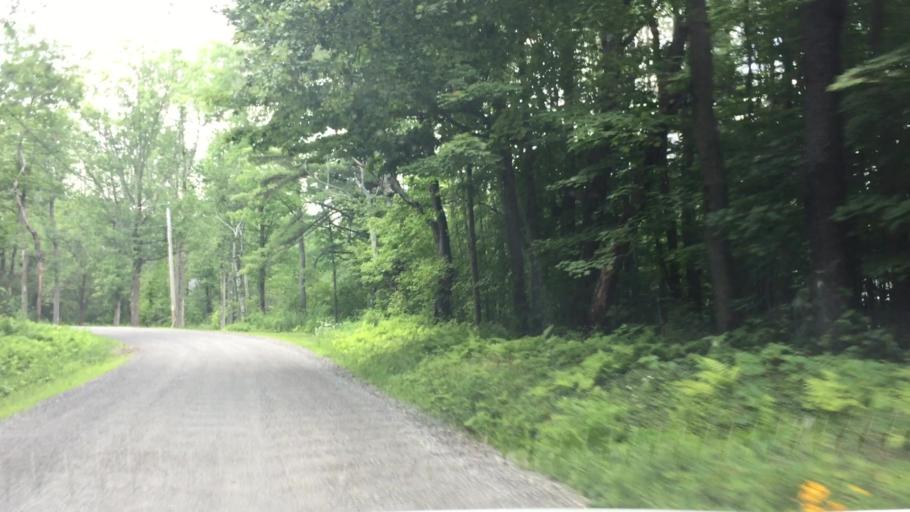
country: US
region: Massachusetts
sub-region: Berkshire County
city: Lee
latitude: 42.2744
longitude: -73.1838
